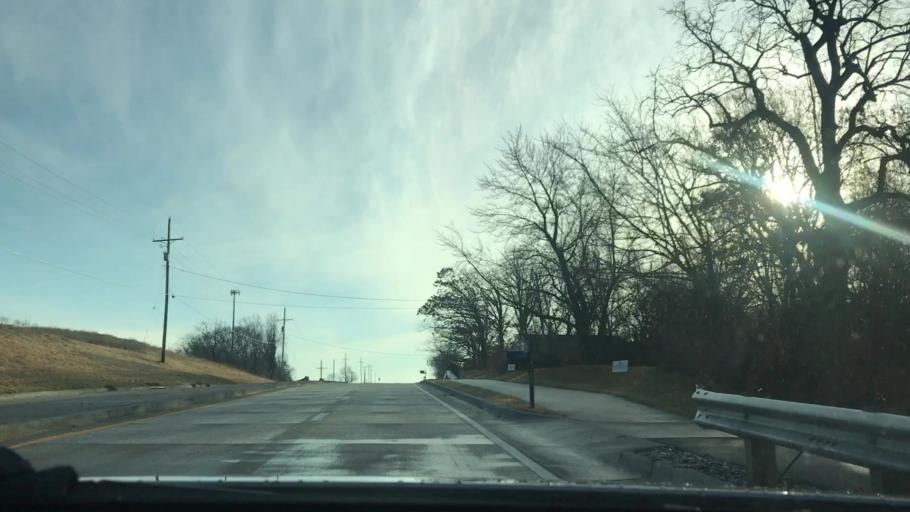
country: US
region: Missouri
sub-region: Platte County
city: Weatherby Lake
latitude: 39.2221
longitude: -94.7423
